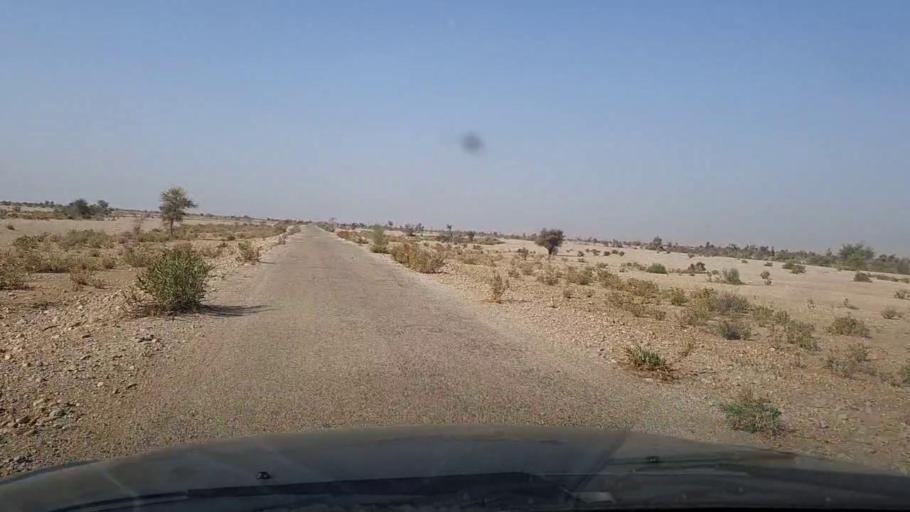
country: PK
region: Sindh
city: Sann
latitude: 25.9219
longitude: 68.0160
